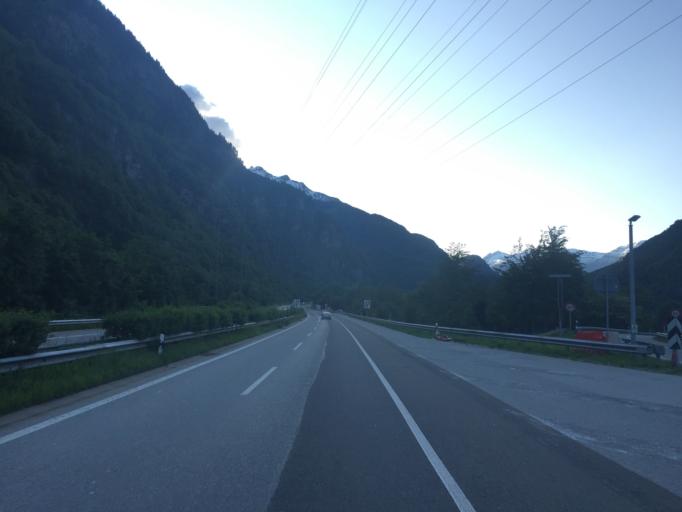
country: CH
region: Ticino
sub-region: Leventina District
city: Bodio
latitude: 46.3900
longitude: 8.8851
